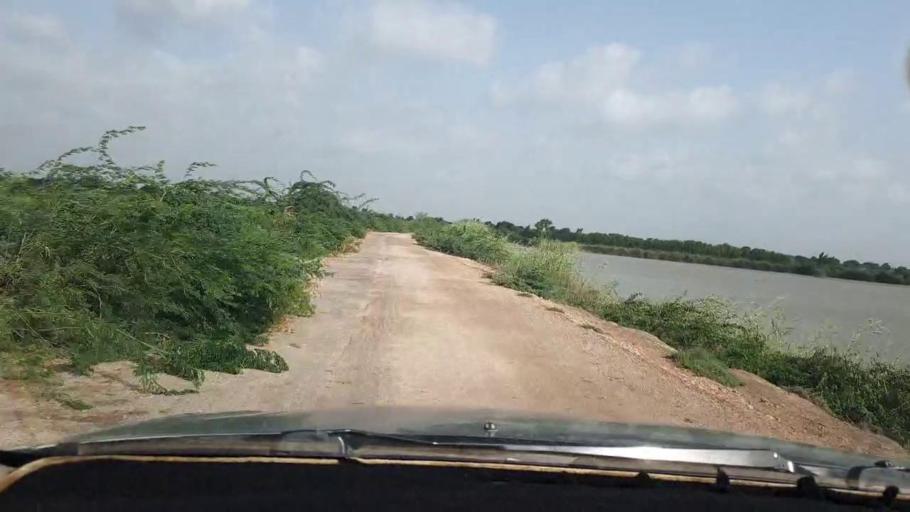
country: PK
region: Sindh
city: Tando Bago
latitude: 24.7775
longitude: 68.9831
